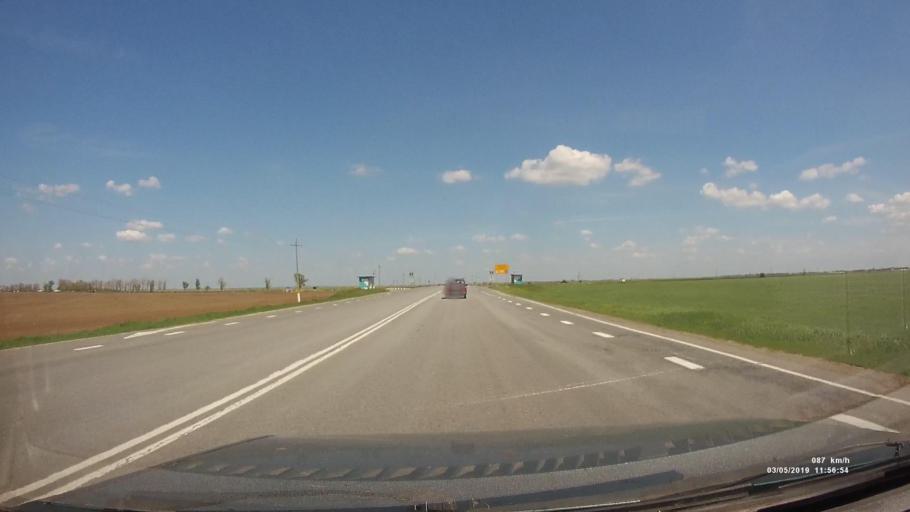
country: RU
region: Rostov
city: Bagayevskaya
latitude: 47.2000
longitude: 40.3054
